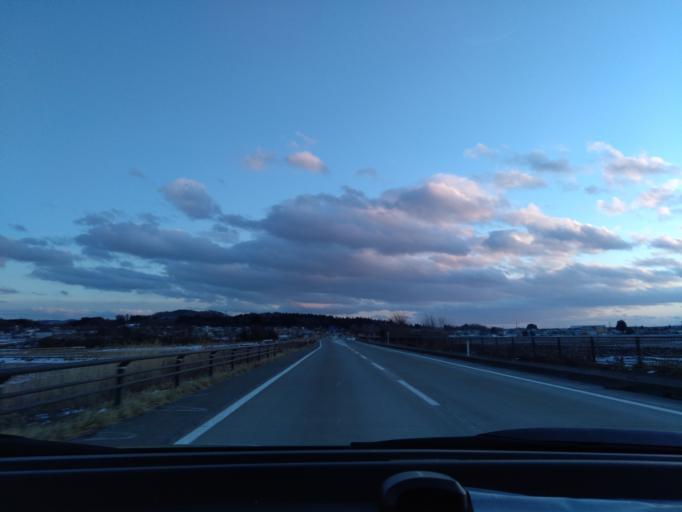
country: JP
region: Iwate
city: Hanamaki
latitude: 39.3951
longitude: 141.1423
